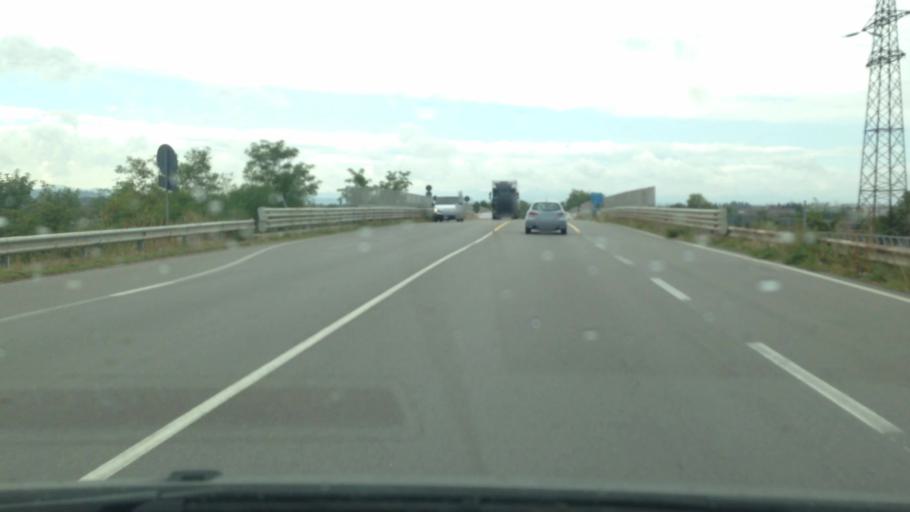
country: IT
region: Piedmont
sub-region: Provincia di Alessandria
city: Tortona
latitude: 44.8963
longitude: 8.8399
